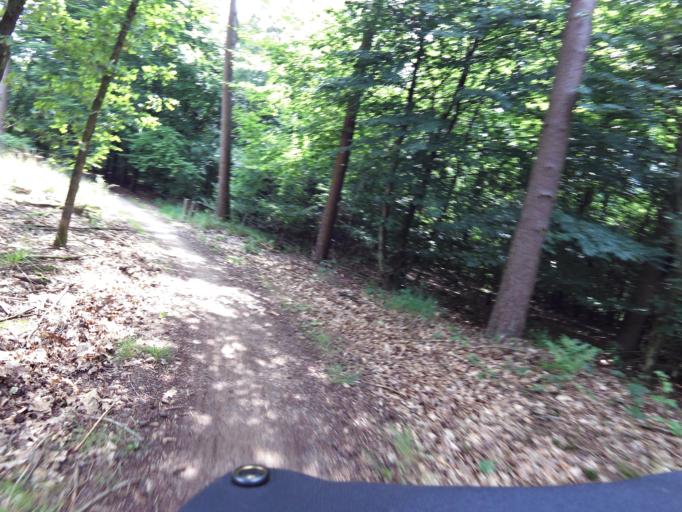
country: NL
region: Limburg
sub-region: Gemeente Roerdalen
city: Vlodrop
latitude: 51.1538
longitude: 6.1078
